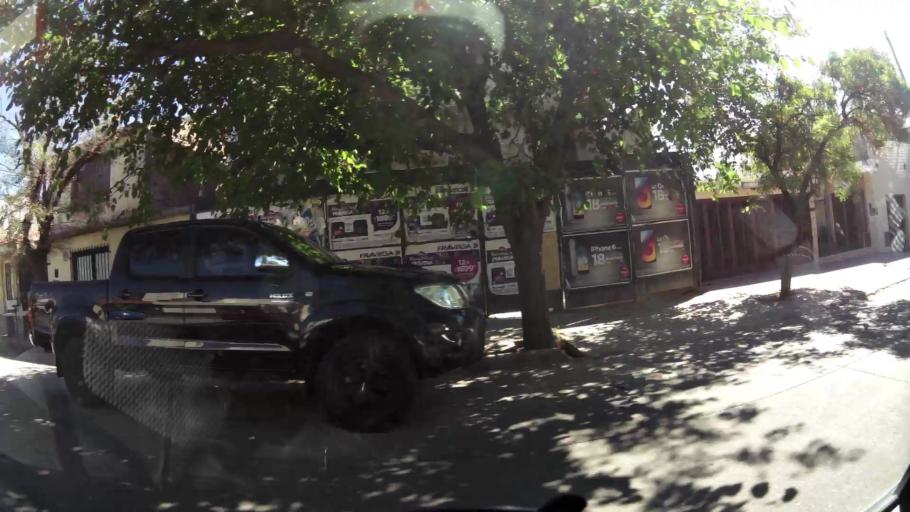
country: AR
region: Mendoza
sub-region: Departamento de Godoy Cruz
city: Godoy Cruz
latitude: -32.9067
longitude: -68.8628
